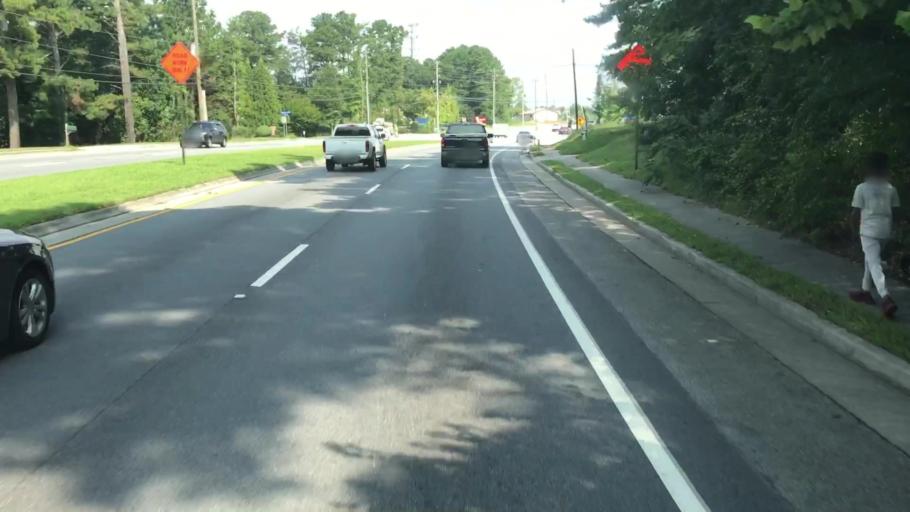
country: US
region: Georgia
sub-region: Gwinnett County
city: Lawrenceville
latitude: 33.9500
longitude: -84.0493
